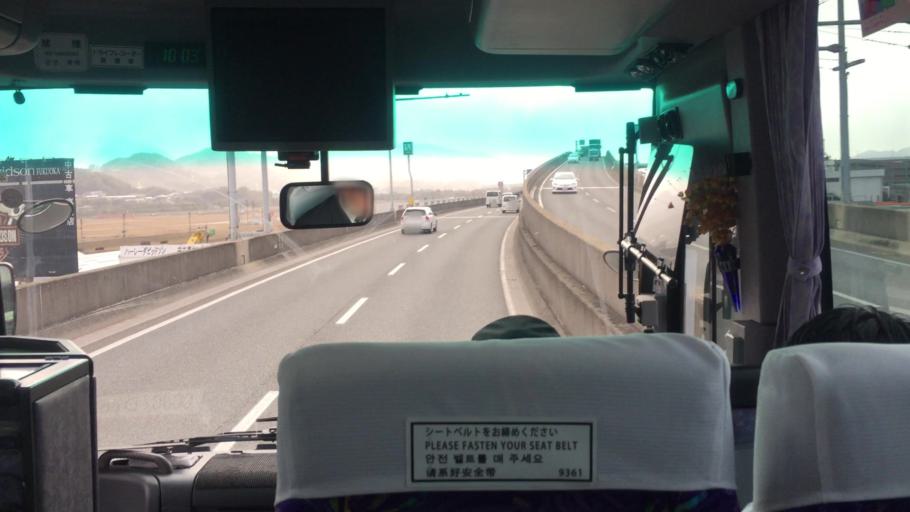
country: JP
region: Fukuoka
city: Fukuoka-shi
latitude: 33.5754
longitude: 130.4515
